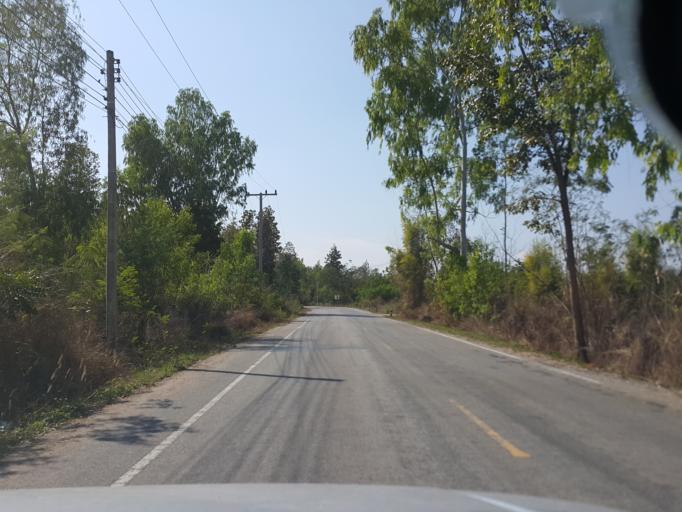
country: TH
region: Chiang Mai
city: Doi Lo
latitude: 18.5348
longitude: 98.8029
